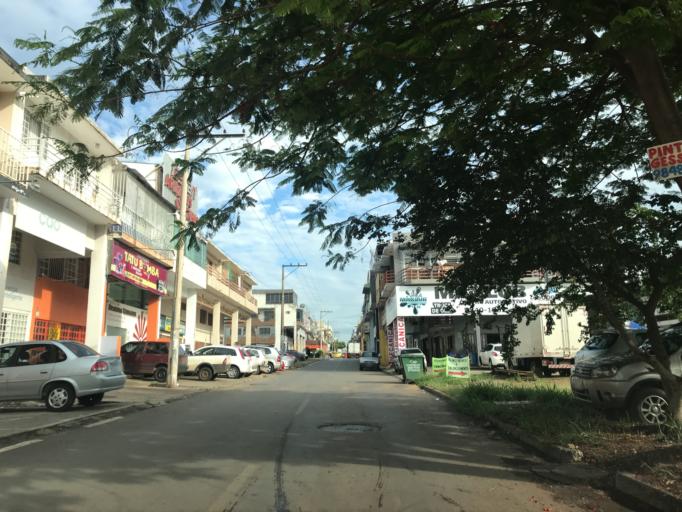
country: BR
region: Federal District
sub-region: Brasilia
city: Brasilia
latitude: -15.7545
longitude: -47.8946
